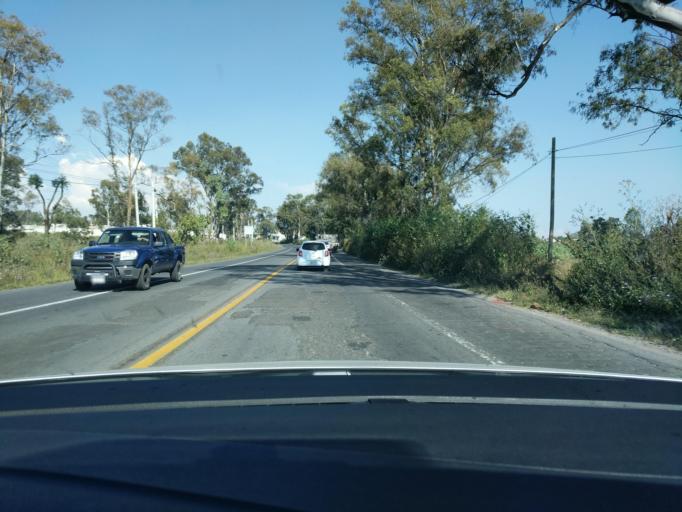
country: MX
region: Puebla
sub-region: Santa Isabel Cholula
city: San Pablo Ahuatempa
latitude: 18.9864
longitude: -98.3618
